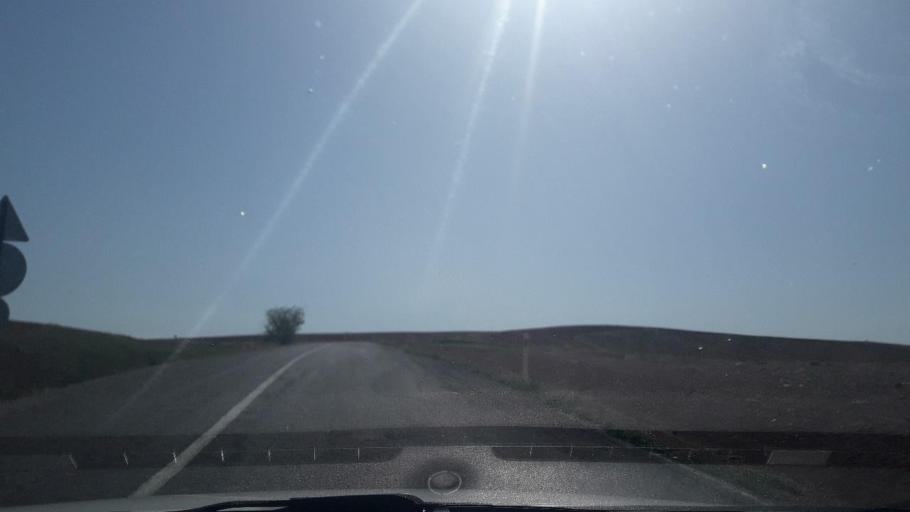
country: TR
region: Sivas
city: Alacahan
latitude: 39.0765
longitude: 37.5507
